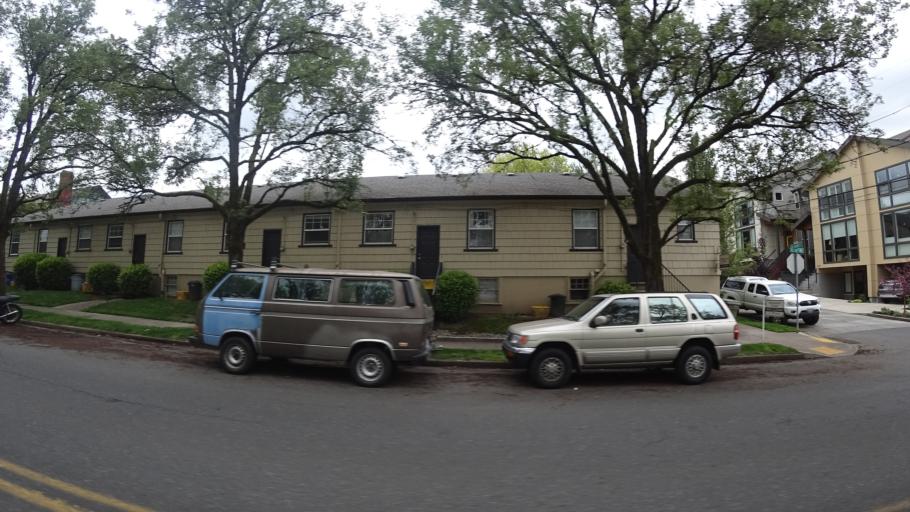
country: US
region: Oregon
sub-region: Clackamas County
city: Milwaukie
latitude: 45.4798
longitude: -122.6484
